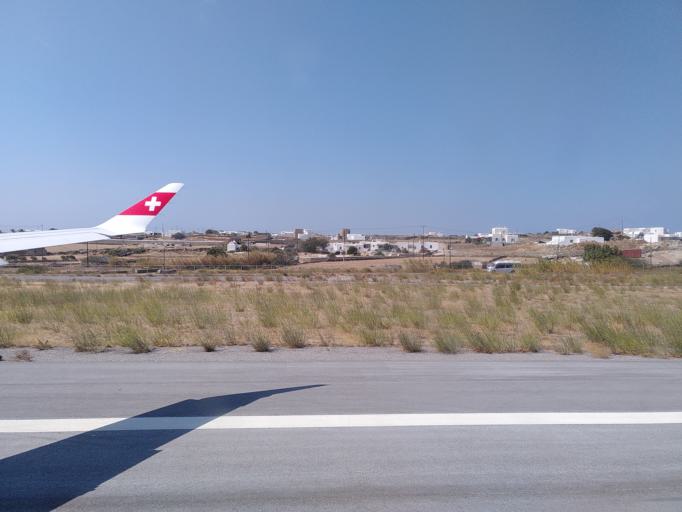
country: GR
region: South Aegean
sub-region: Nomos Kykladon
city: Mykonos
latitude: 37.4293
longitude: 25.3508
